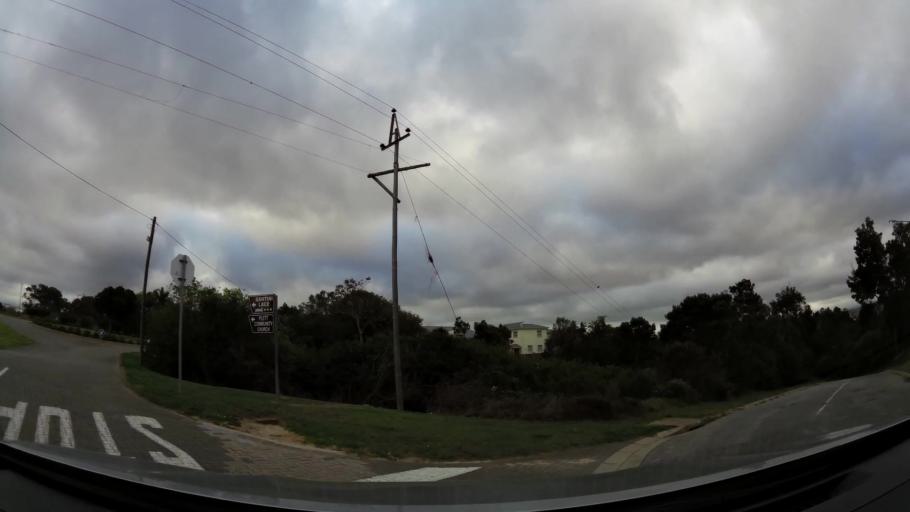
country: ZA
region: Western Cape
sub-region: Eden District Municipality
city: Plettenberg Bay
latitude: -34.0483
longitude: 23.3622
